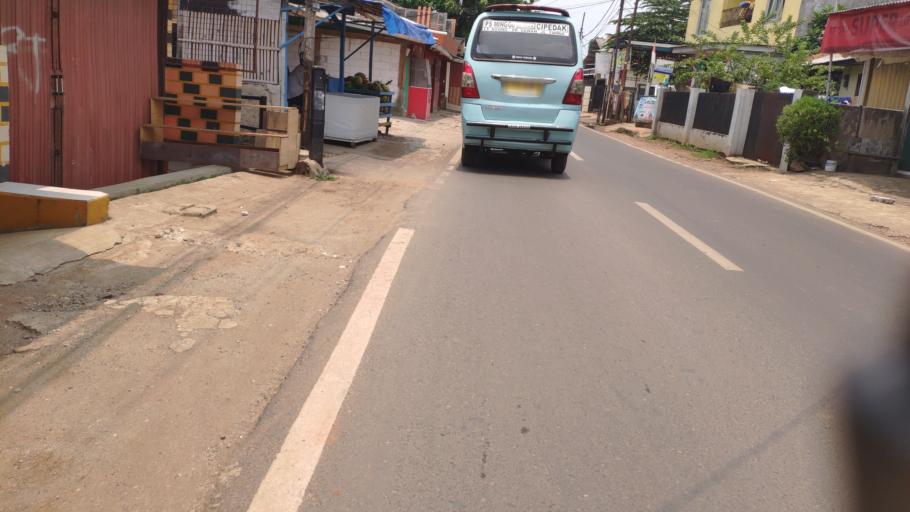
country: ID
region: West Java
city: Depok
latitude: -6.3493
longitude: 106.8199
